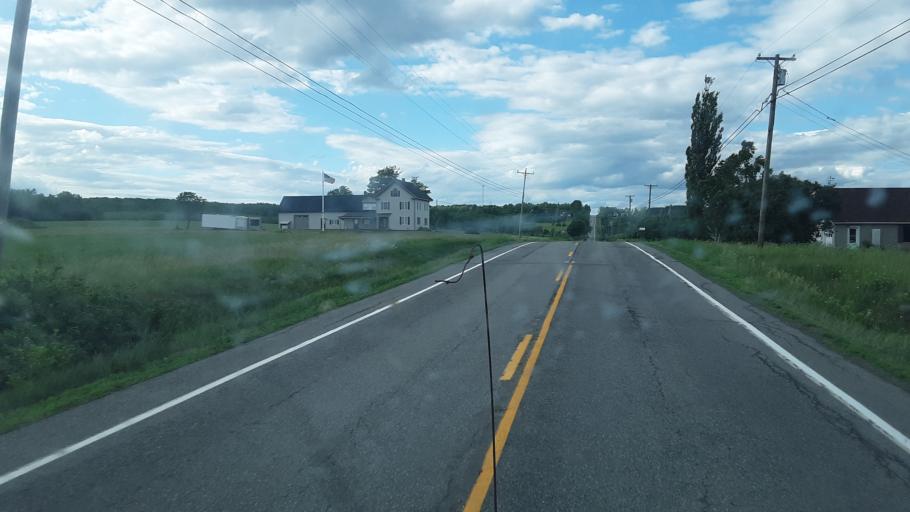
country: US
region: Maine
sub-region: Penobscot County
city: Patten
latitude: 46.0167
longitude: -68.4458
